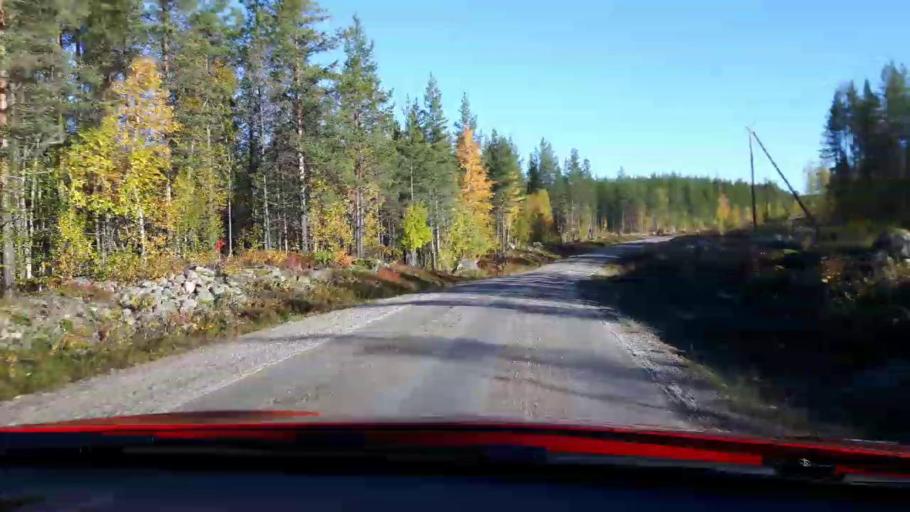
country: SE
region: Jaemtland
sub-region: Stroemsunds Kommun
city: Stroemsund
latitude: 64.3799
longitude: 15.1485
